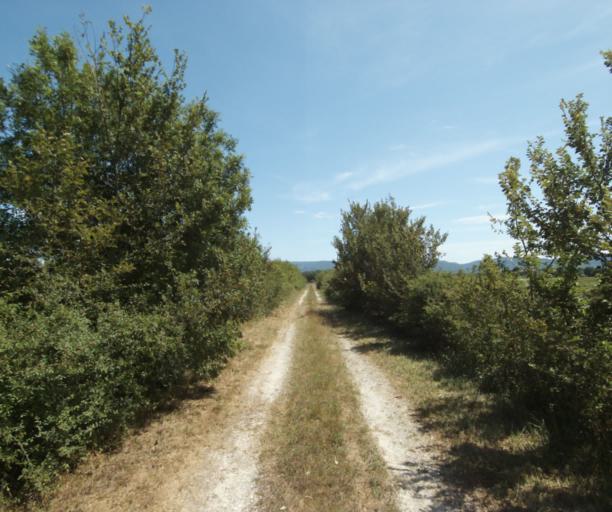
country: FR
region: Midi-Pyrenees
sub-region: Departement de la Haute-Garonne
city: Revel
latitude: 43.5001
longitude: 2.0142
